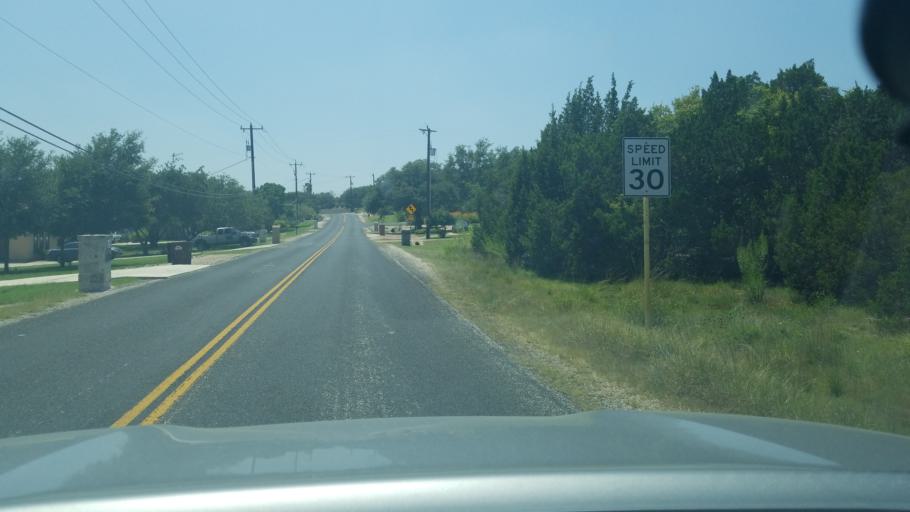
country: US
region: Texas
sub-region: Bexar County
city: Timberwood Park
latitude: 29.6795
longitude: -98.5121
